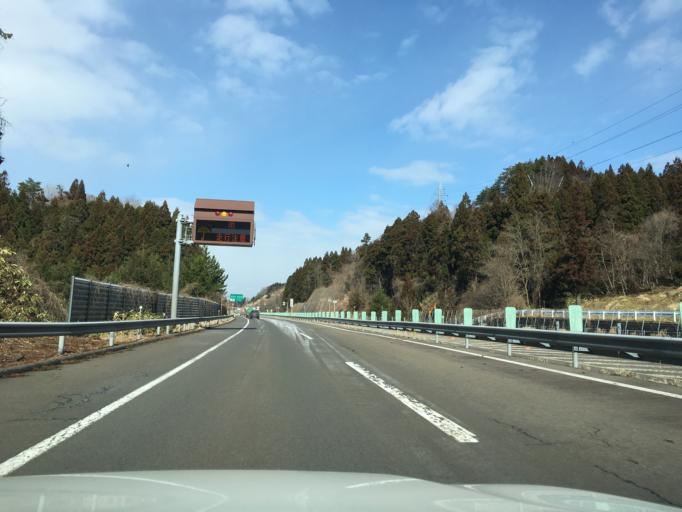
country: JP
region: Akita
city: Akita
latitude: 39.7776
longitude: 140.1175
